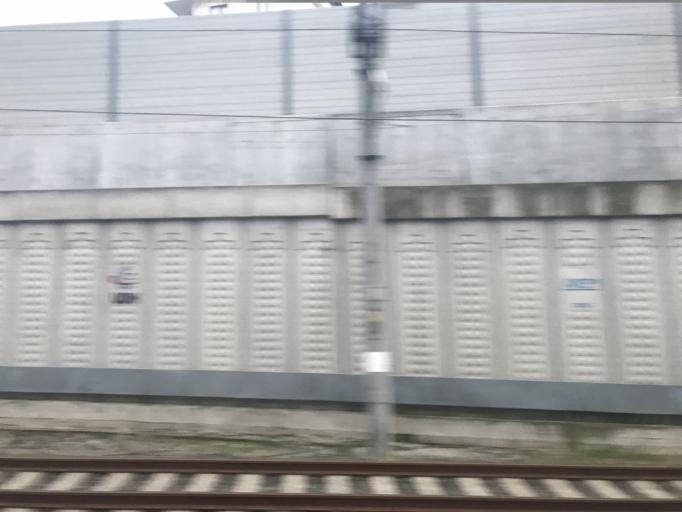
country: TR
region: Istanbul
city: Pendik
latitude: 40.8591
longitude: 29.2744
